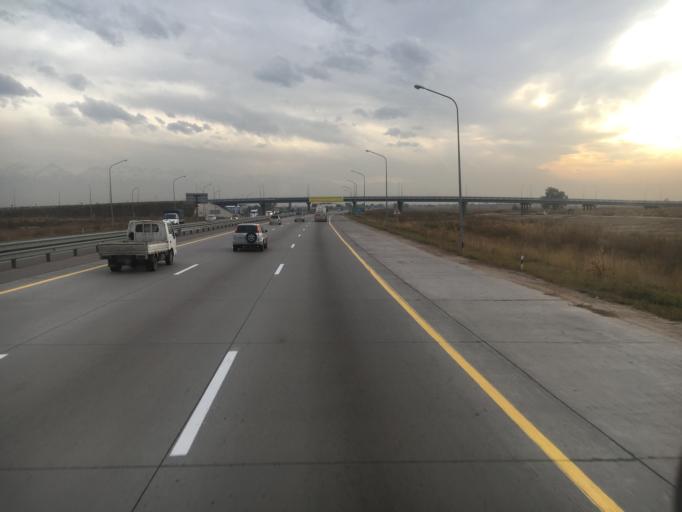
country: KZ
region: Almaty Oblysy
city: Pervomayskiy
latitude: 43.3934
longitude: 76.9732
